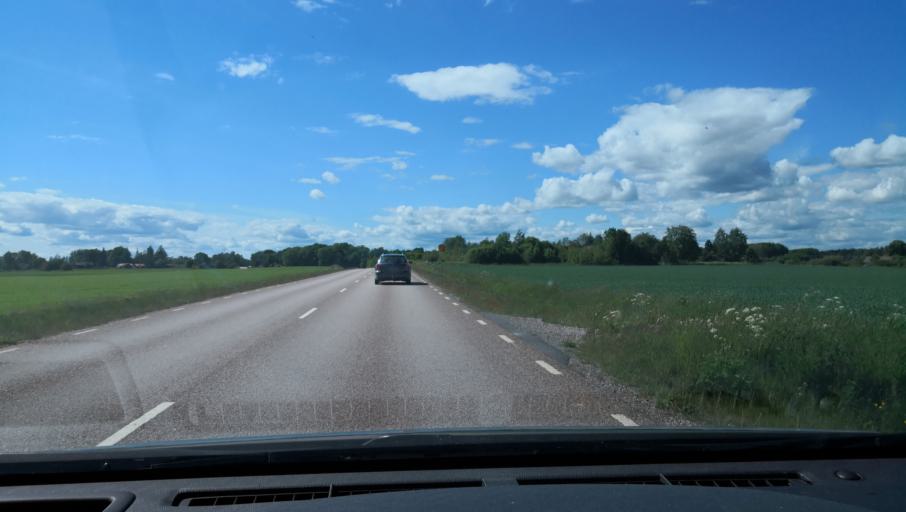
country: SE
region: Vaestmanland
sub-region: Kungsors Kommun
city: Kungsoer
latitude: 59.2892
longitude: 16.0981
